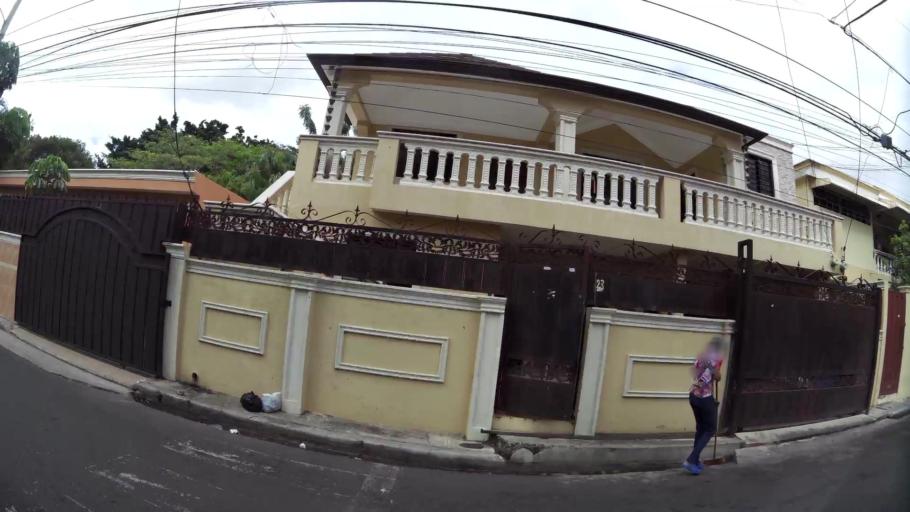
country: DO
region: Santiago
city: Santiago de los Caballeros
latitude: 19.4631
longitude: -70.6699
